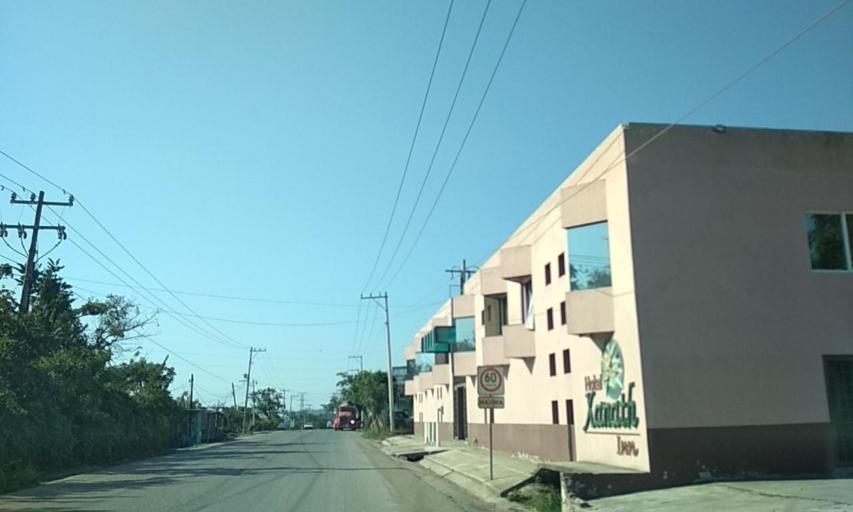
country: MX
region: Veracruz
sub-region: Papantla
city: El Chote
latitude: 20.4074
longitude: -97.3452
